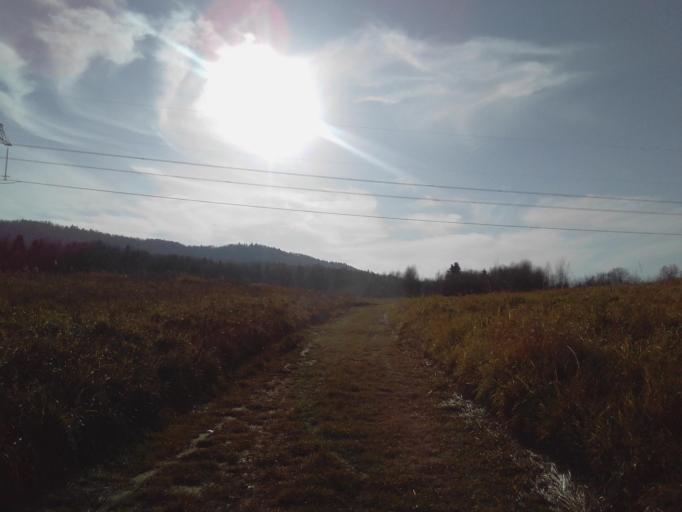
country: PL
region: Subcarpathian Voivodeship
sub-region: Powiat strzyzowski
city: Jawornik
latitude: 49.8000
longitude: 21.8866
